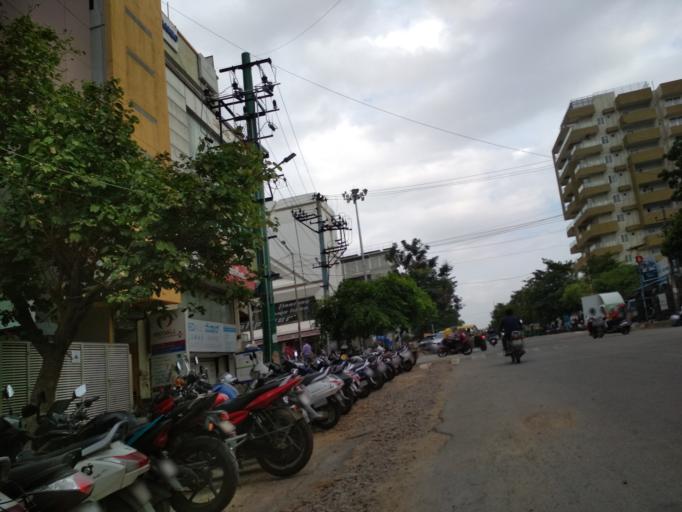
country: IN
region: Karnataka
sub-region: Bangalore Urban
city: Bangalore
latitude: 12.9199
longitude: 77.6451
